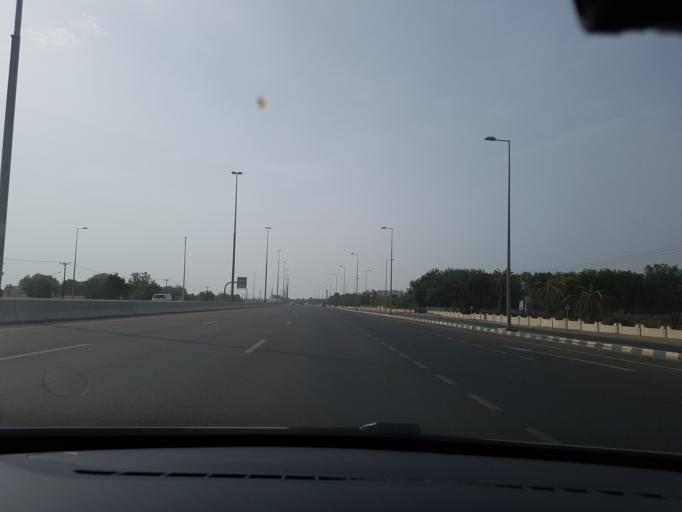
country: OM
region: Al Batinah
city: Al Sohar
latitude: 24.3347
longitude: 56.7376
